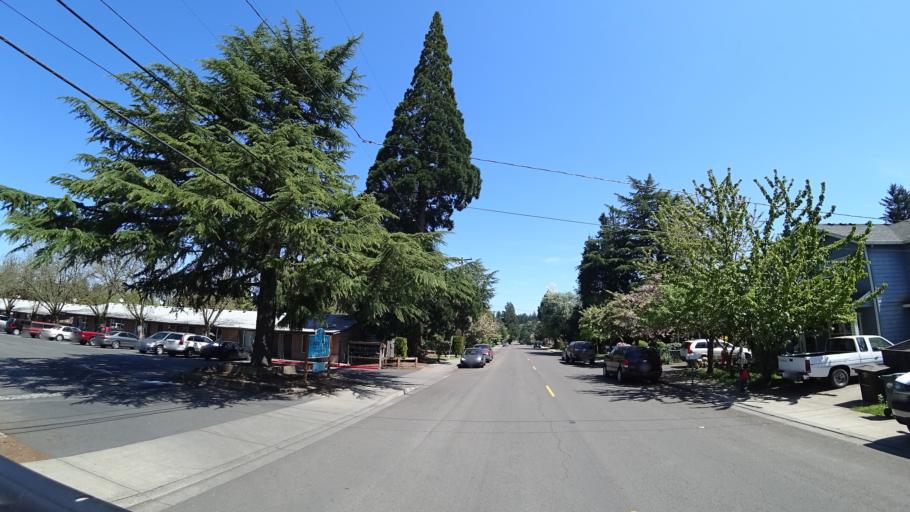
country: US
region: Oregon
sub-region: Washington County
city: Hillsboro
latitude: 45.5187
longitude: -122.9663
